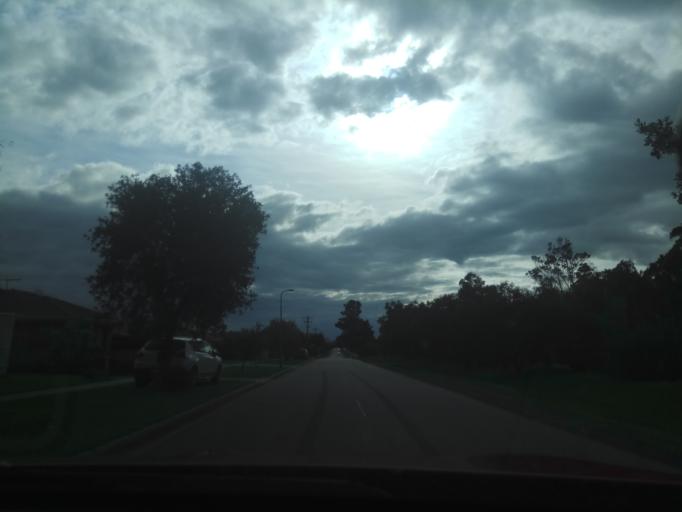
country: AU
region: Victoria
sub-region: Casey
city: Cranbourne North
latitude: -38.0752
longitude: 145.2799
